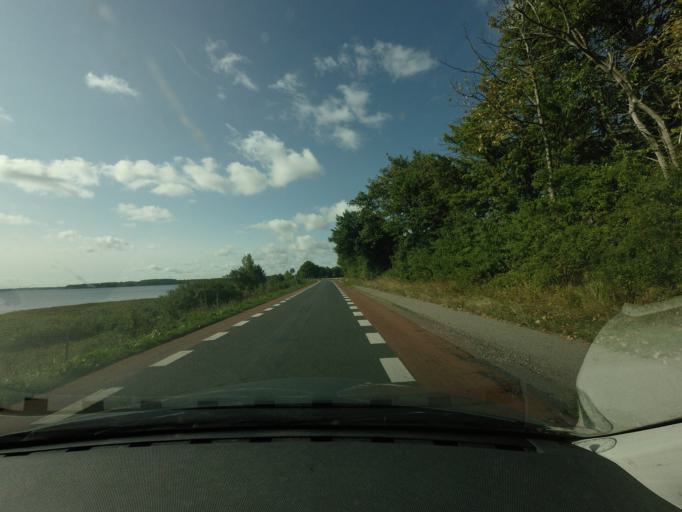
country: DK
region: Zealand
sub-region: Vordingborg Kommune
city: Praesto
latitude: 55.1615
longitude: 12.0213
